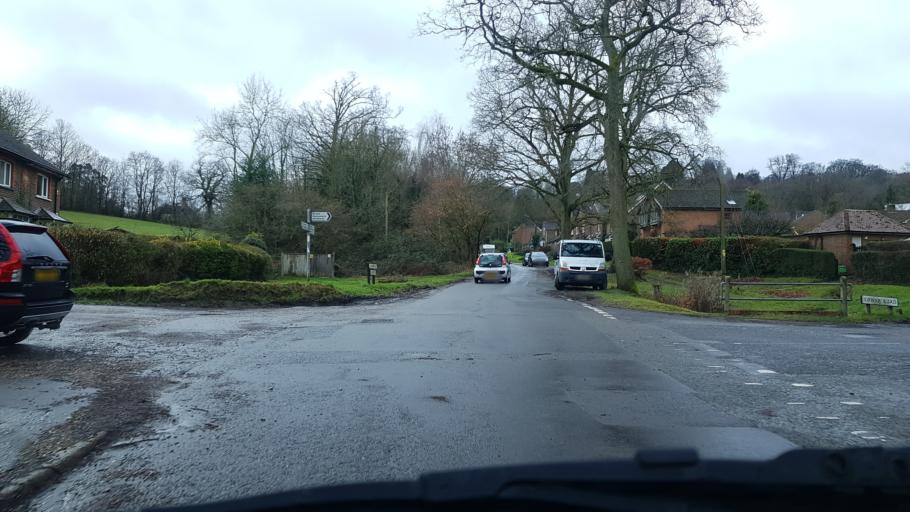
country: GB
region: England
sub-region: Surrey
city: Haslemere
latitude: 51.1022
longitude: -0.6855
